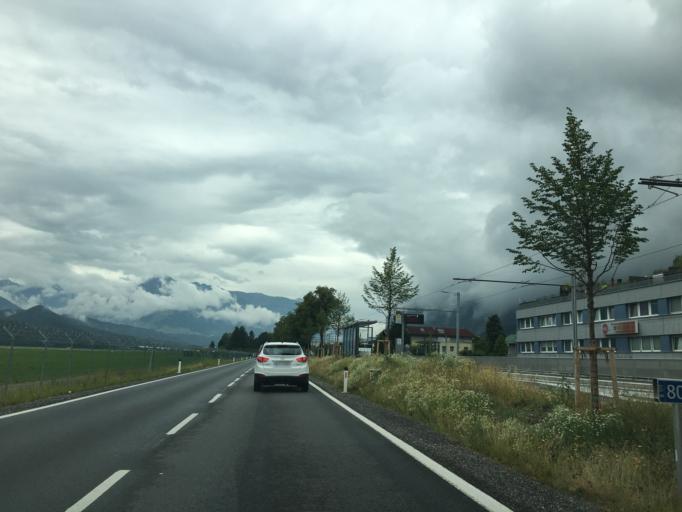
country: AT
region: Tyrol
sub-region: Politischer Bezirk Innsbruck Land
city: Vols
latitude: 47.2634
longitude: 11.3576
